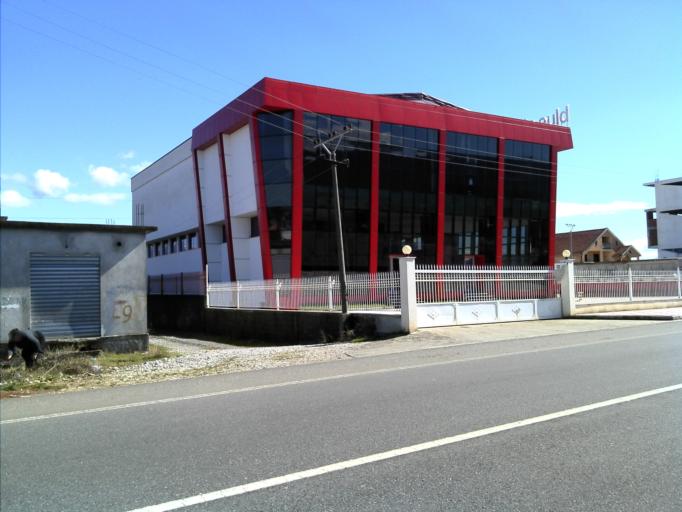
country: AL
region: Shkoder
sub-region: Rrethi i Shkodres
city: Shkoder
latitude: 42.0973
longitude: 19.5060
